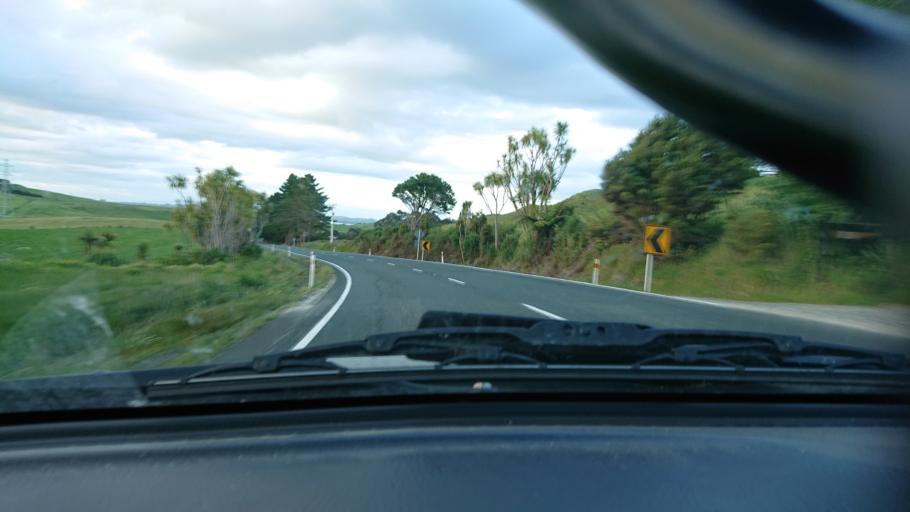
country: NZ
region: Auckland
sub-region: Auckland
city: Parakai
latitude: -36.4714
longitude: 174.4496
